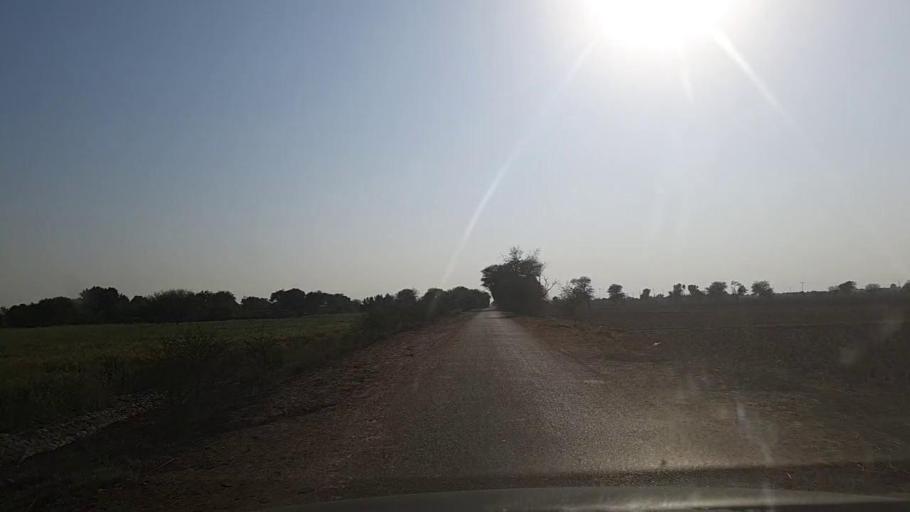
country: PK
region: Sindh
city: Naukot
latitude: 25.0084
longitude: 69.2769
